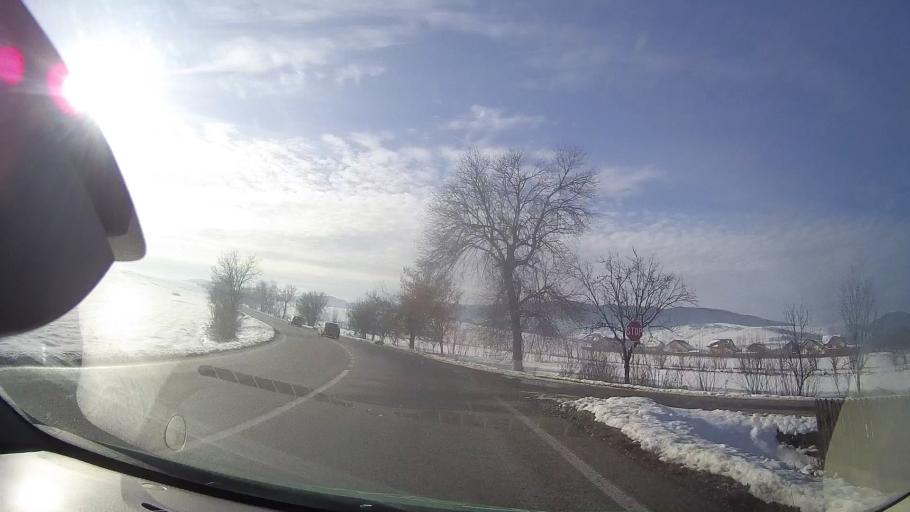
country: RO
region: Neamt
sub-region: Comuna Garcina
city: Garcina
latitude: 46.9981
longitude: 26.3688
